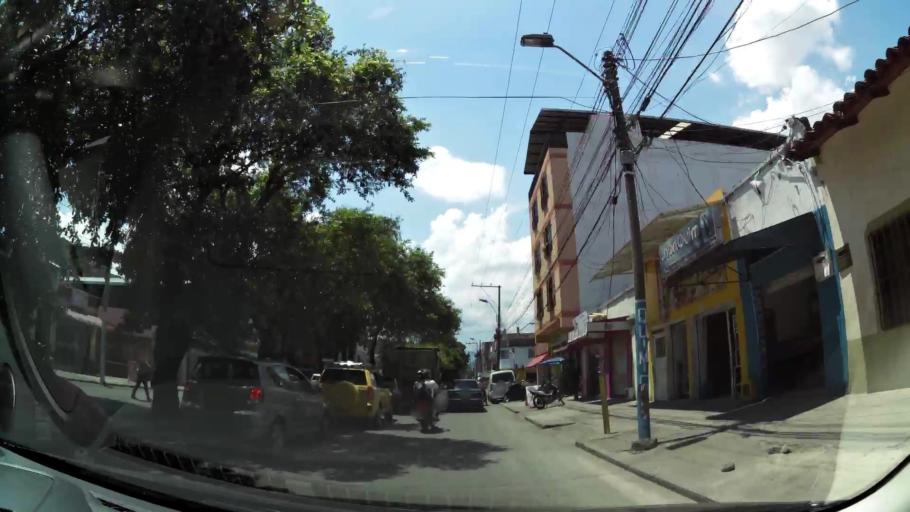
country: CO
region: Valle del Cauca
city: Cali
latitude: 3.4484
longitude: -76.4986
